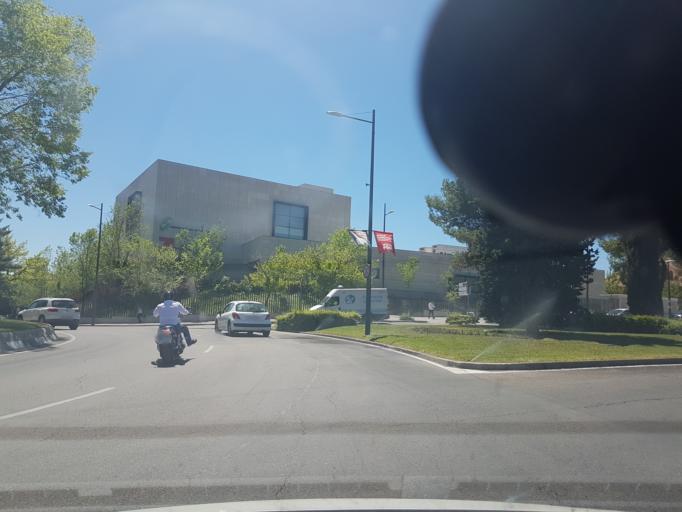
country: ES
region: Madrid
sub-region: Provincia de Madrid
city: Pozuelo de Alarcon
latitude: 40.4356
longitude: -3.7991
